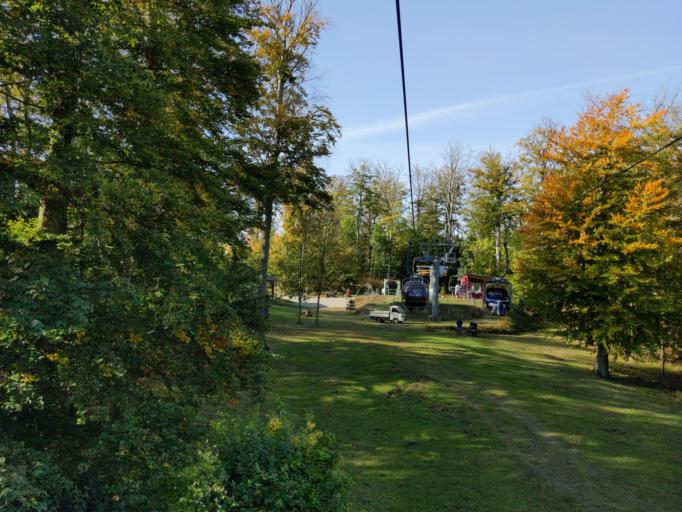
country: DE
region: Saxony-Anhalt
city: Thale
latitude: 51.7416
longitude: 11.0187
